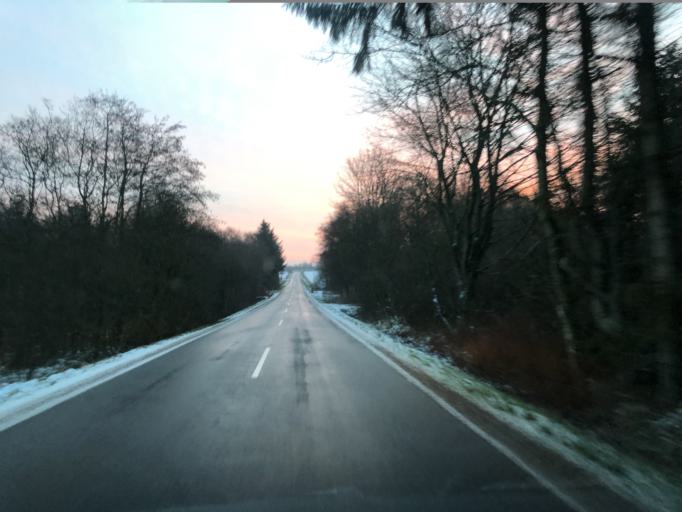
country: DK
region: Central Jutland
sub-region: Holstebro Kommune
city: Ulfborg
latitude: 56.2014
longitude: 8.4376
